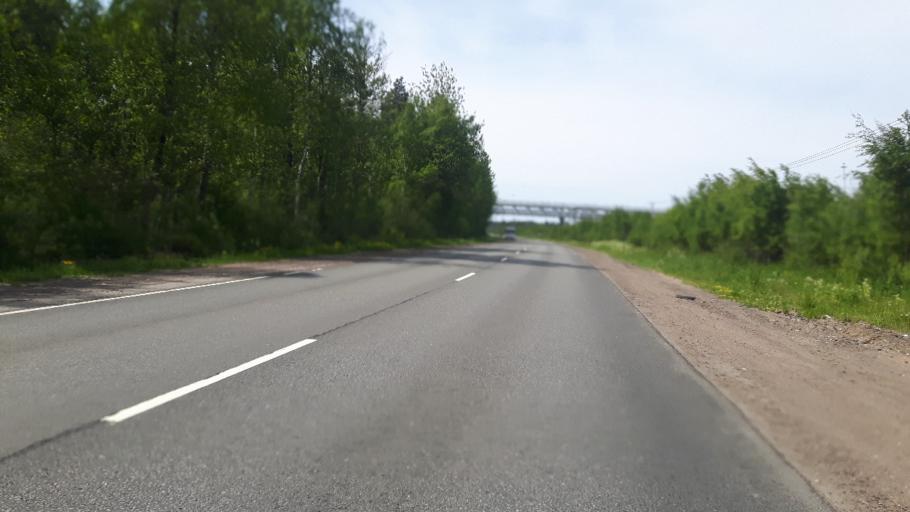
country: RU
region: Leningrad
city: Ust'-Luga
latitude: 59.6562
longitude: 28.3878
